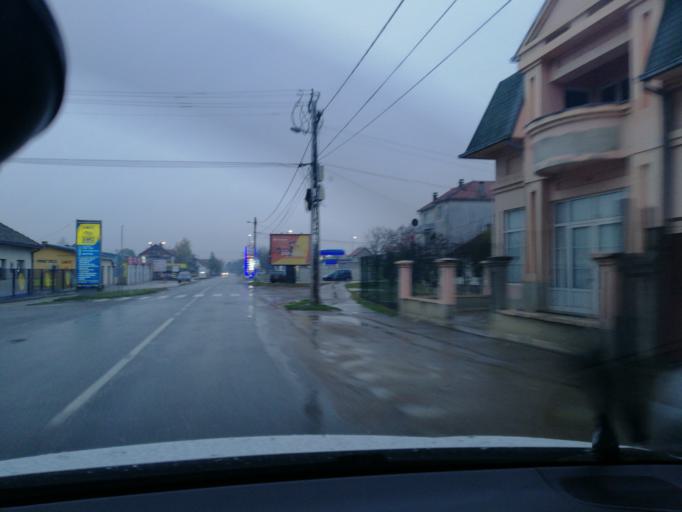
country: RS
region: Autonomna Pokrajina Vojvodina
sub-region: Sremski Okrug
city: Ruma
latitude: 45.0026
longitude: 19.8159
